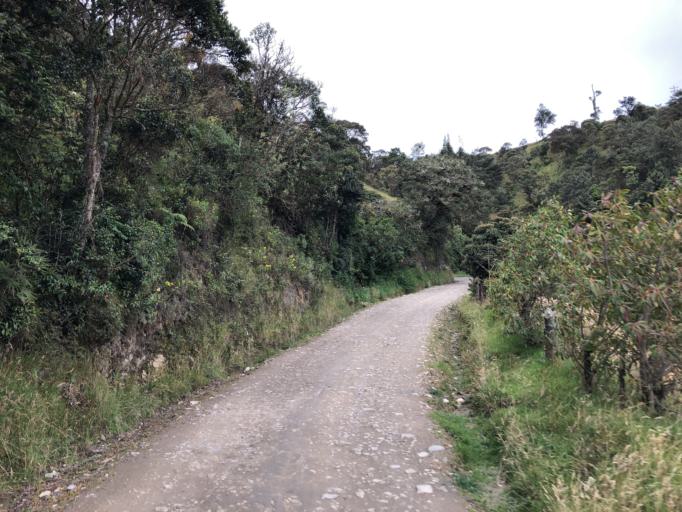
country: CO
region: Cauca
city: Totoro
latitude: 2.4985
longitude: -76.3561
